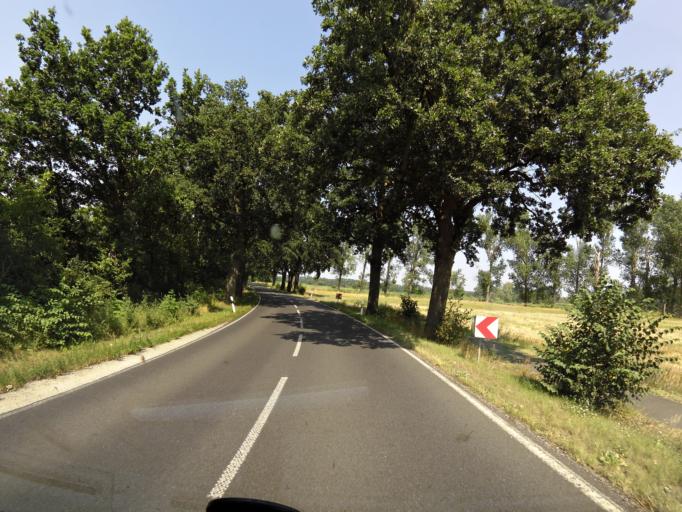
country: DE
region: Brandenburg
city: Liebenwalde
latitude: 52.8541
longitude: 13.3316
